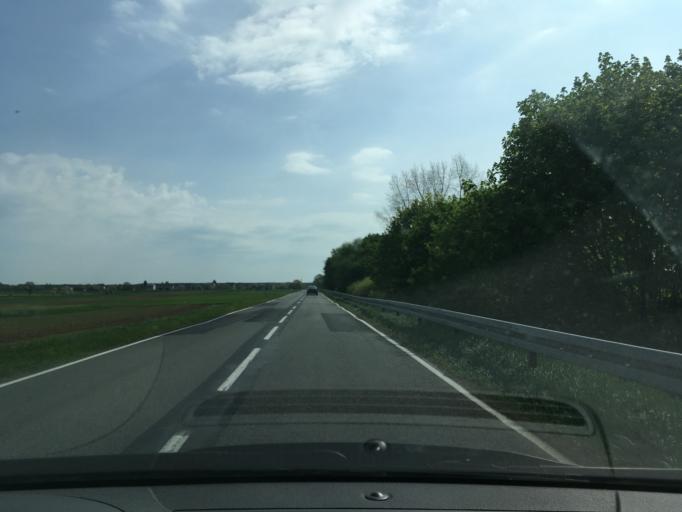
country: PL
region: Lublin Voivodeship
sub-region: Powiat rycki
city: Deblin
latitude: 51.4767
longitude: 21.8793
